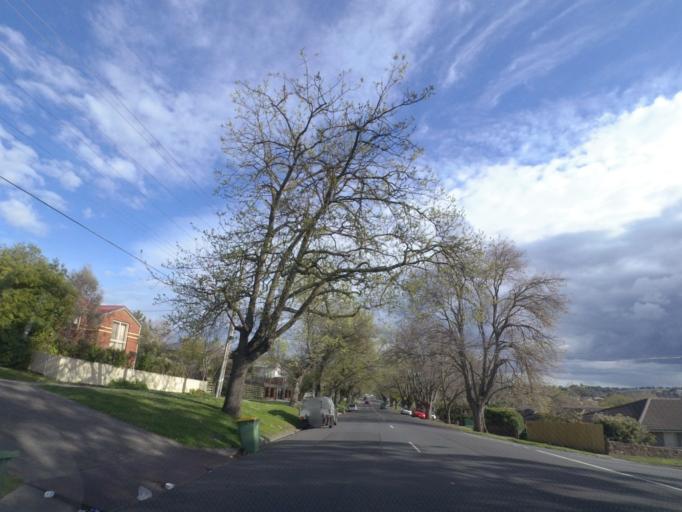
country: AU
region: Victoria
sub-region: Yarra Ranges
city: Lilydale
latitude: -37.7534
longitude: 145.3559
